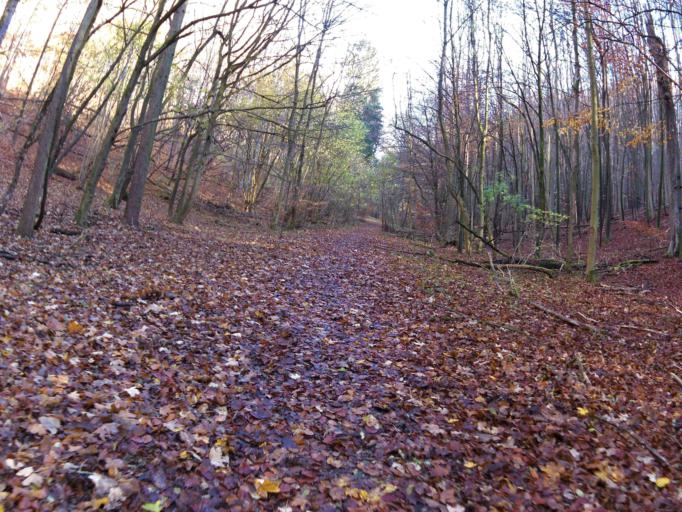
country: DE
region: Thuringia
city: Kammerforst
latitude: 51.0683
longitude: 10.4322
